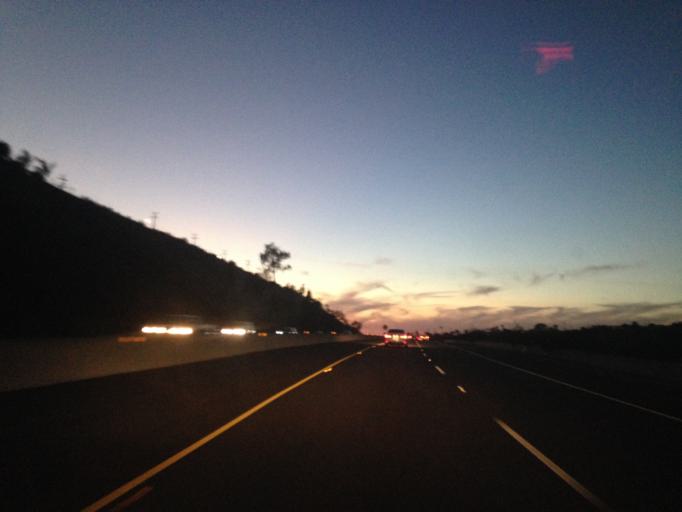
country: US
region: California
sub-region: San Diego County
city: Camp Pendleton South
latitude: 33.2125
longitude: -117.3680
